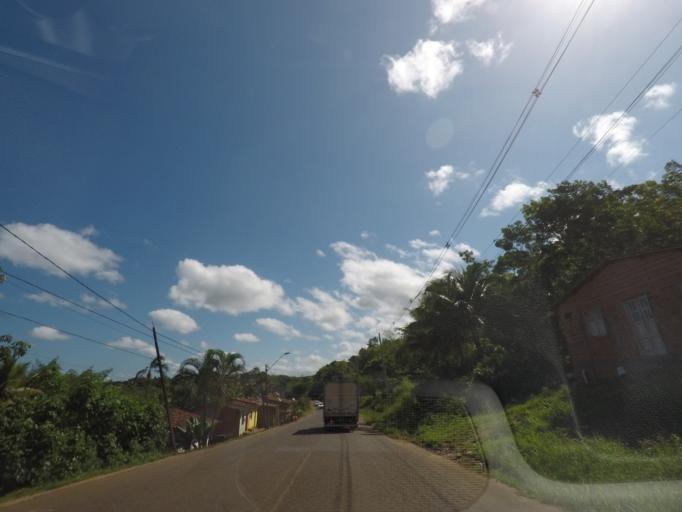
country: BR
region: Bahia
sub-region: Itubera
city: Itubera
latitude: -13.7532
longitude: -39.1541
